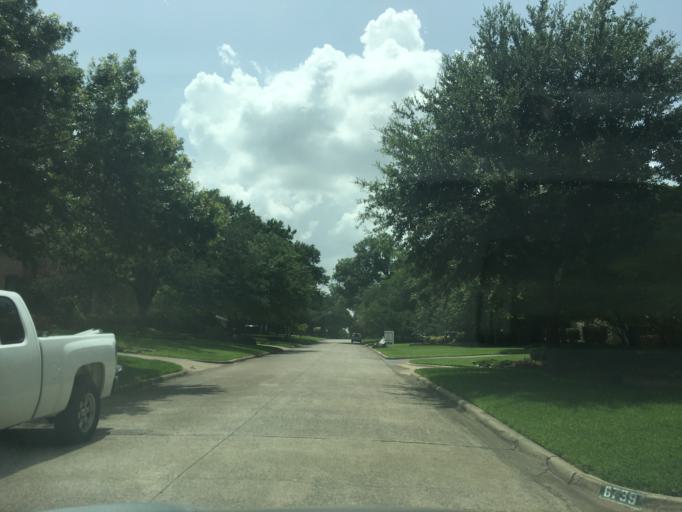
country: US
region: Texas
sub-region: Dallas County
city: University Park
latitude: 32.8894
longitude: -96.7883
